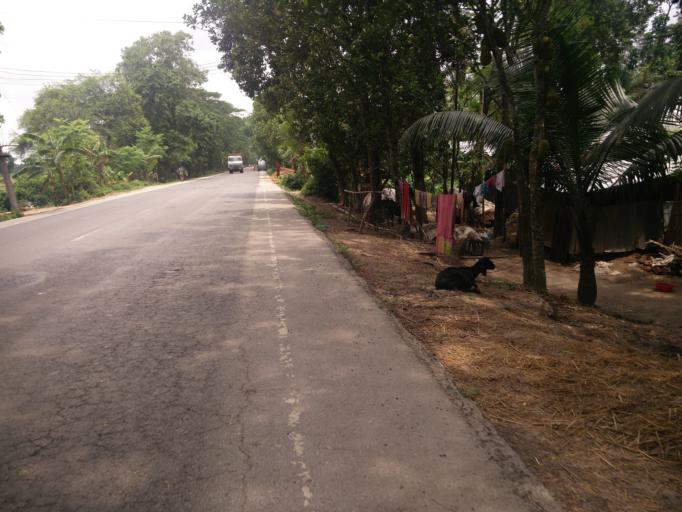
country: BD
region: Khulna
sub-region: Magura
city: Magura
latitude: 23.5451
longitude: 89.5284
